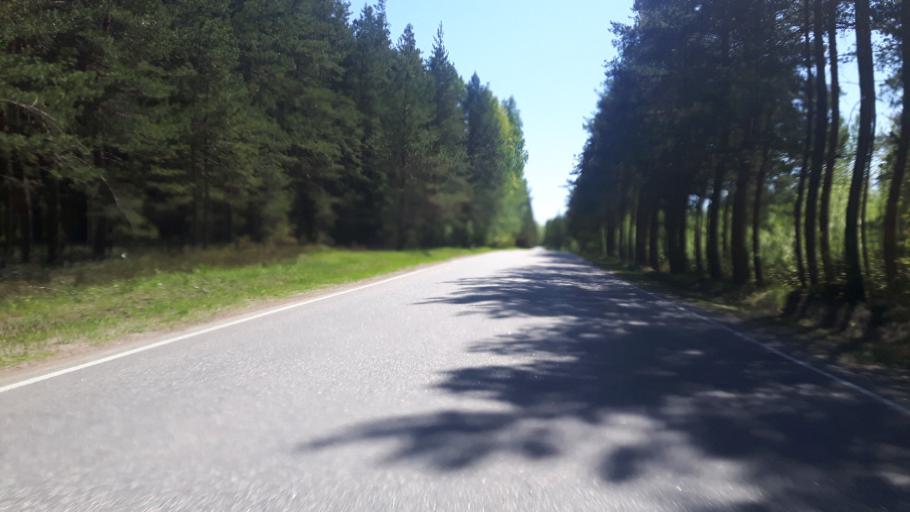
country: RU
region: Leningrad
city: Glebychevo
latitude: 60.3532
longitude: 28.8154
